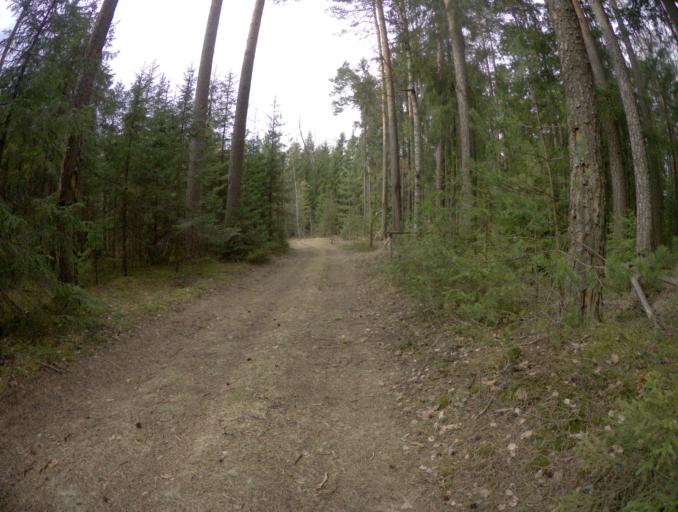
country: RU
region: Vladimir
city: Raduzhnyy
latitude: 55.9364
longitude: 40.2579
